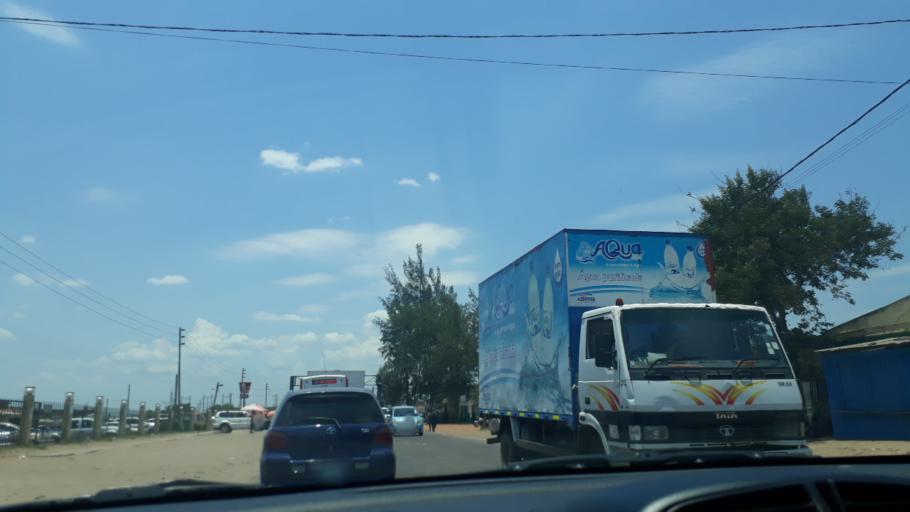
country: MZ
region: Maputo City
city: Maputo
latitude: -25.8877
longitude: 32.6037
